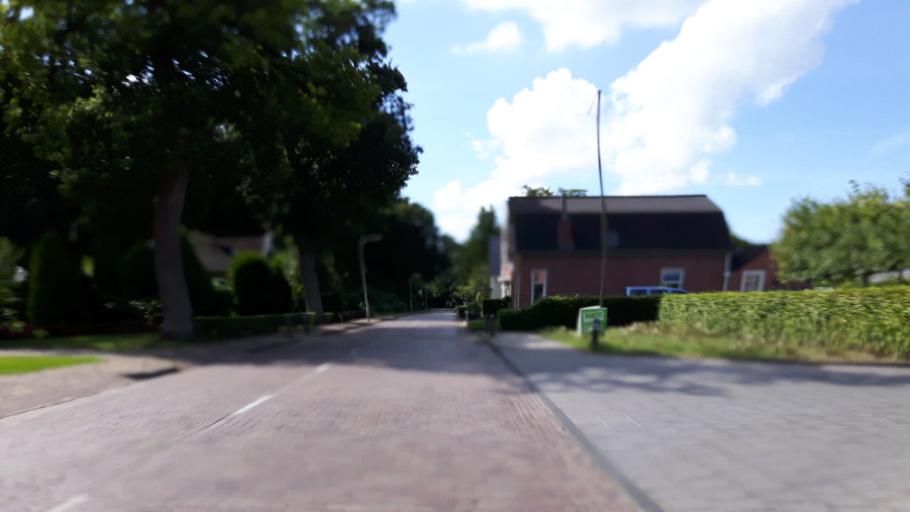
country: NL
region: Friesland
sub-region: Gemeente Smallingerland
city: Drachtstercompagnie
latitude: 53.0802
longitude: 6.2553
